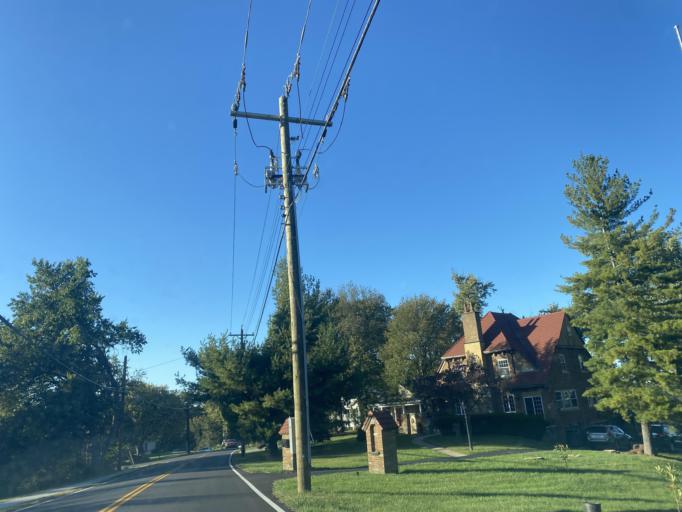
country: US
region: Kentucky
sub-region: Campbell County
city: Dayton
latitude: 39.1068
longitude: -84.4580
